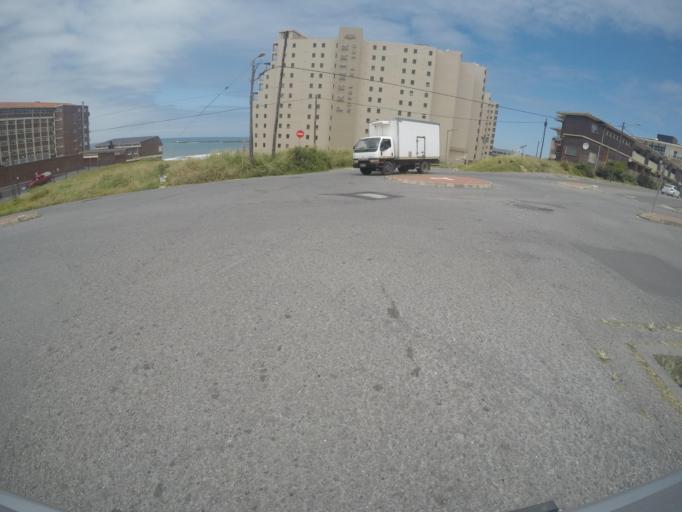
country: ZA
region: Eastern Cape
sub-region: Buffalo City Metropolitan Municipality
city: East London
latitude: -33.0171
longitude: 27.9188
